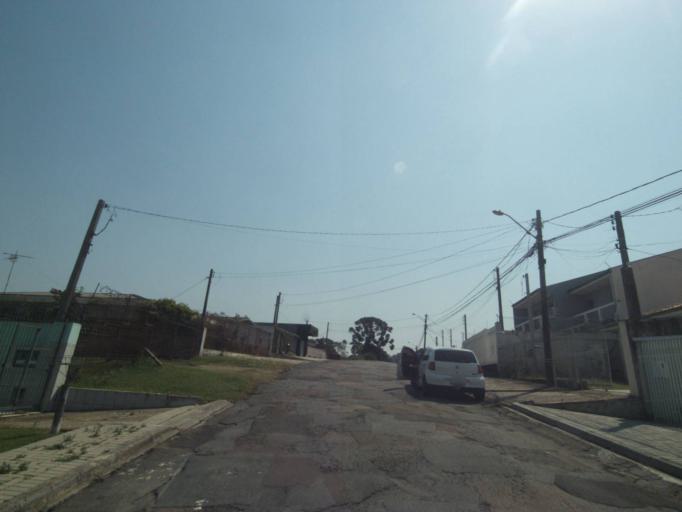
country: BR
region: Parana
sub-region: Sao Jose Dos Pinhais
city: Sao Jose dos Pinhais
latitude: -25.5006
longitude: -49.2740
